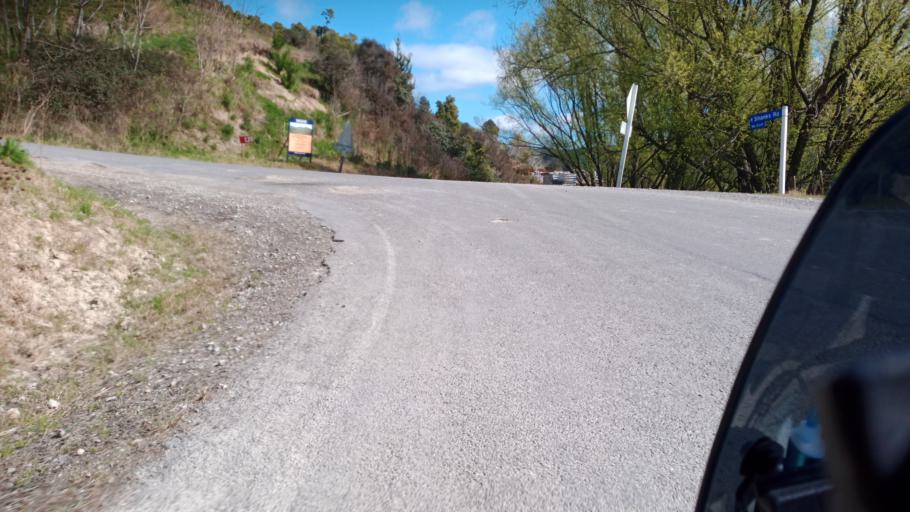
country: NZ
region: Gisborne
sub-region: Gisborne District
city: Gisborne
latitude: -38.7875
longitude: 177.7819
